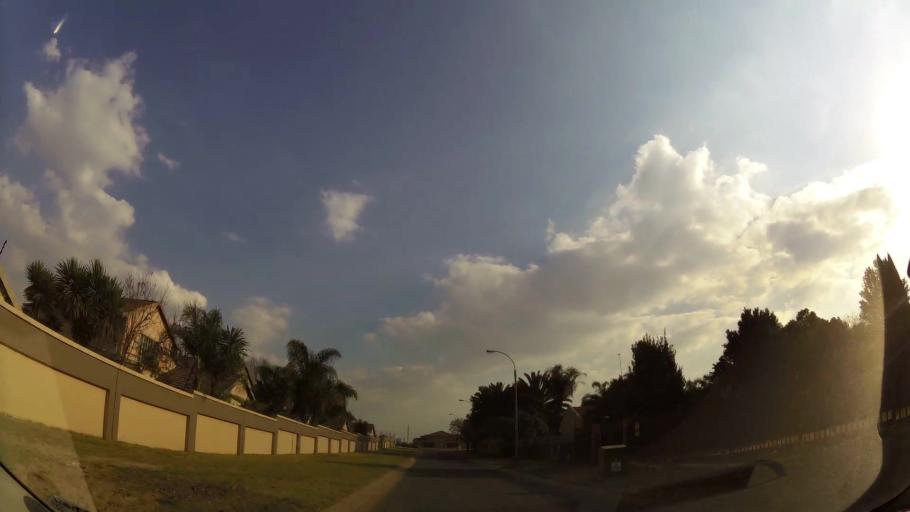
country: ZA
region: Gauteng
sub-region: Ekurhuleni Metropolitan Municipality
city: Benoni
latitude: -26.1093
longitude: 28.2886
